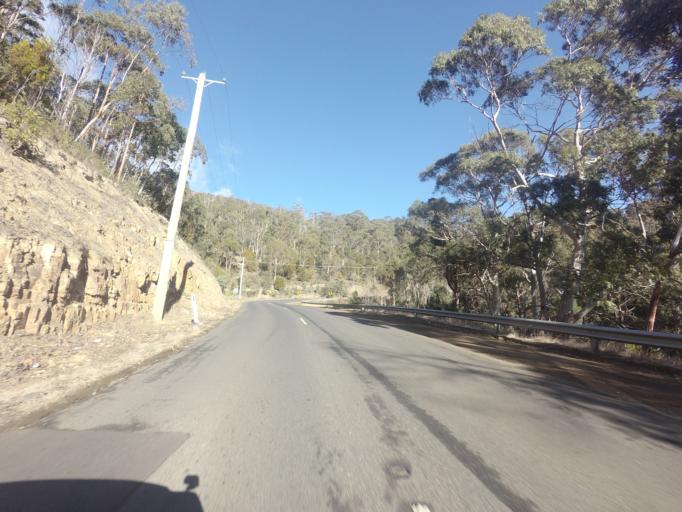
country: AU
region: Tasmania
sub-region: Glenorchy
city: Berriedale
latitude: -42.8259
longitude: 147.2091
